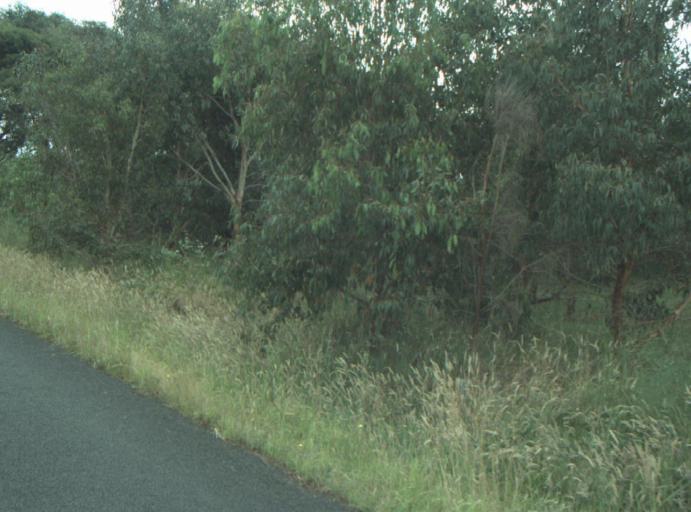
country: AU
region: Victoria
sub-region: Greater Geelong
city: Clifton Springs
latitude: -38.2161
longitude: 144.5599
